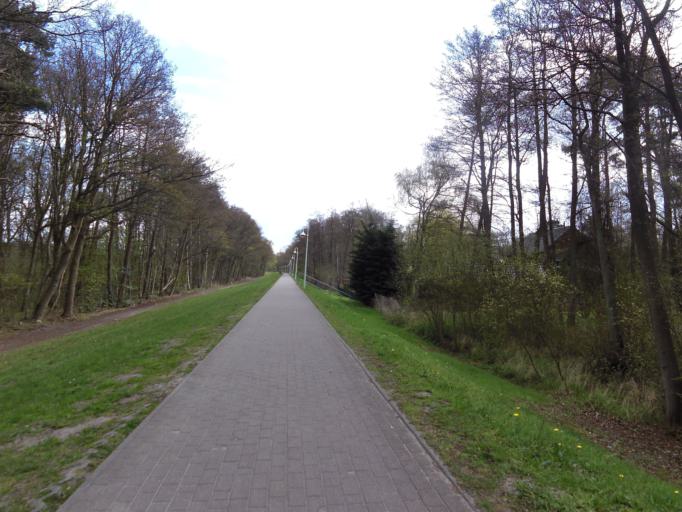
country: DE
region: Mecklenburg-Vorpommern
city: Ostseebad Prerow
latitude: 54.4488
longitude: 12.5695
